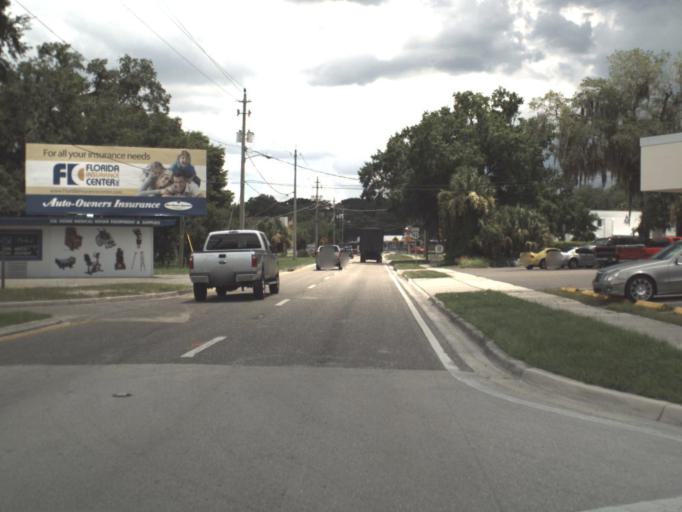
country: US
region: Florida
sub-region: Hillsborough County
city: Plant City
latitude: 28.0164
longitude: -82.1378
